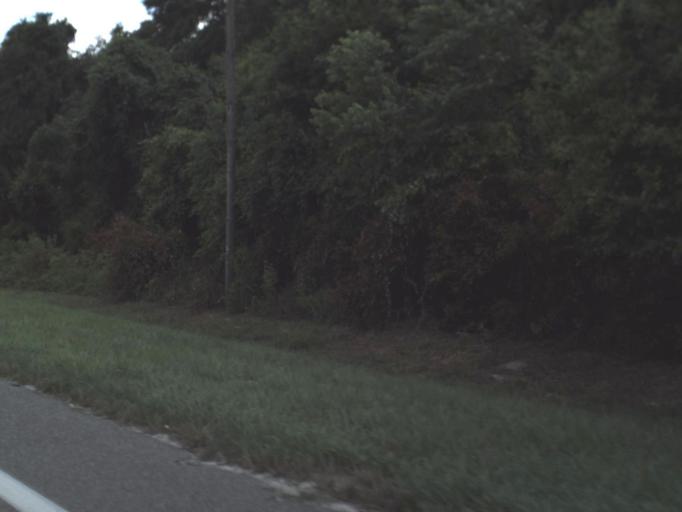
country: US
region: Florida
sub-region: Lafayette County
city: Mayo
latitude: 29.9942
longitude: -83.0123
